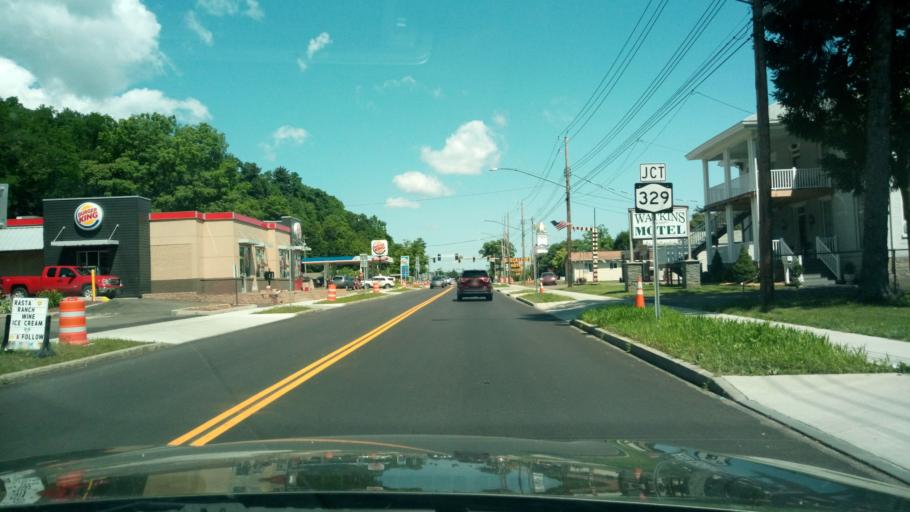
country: US
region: New York
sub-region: Schuyler County
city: Watkins Glen
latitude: 42.3742
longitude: -76.8700
